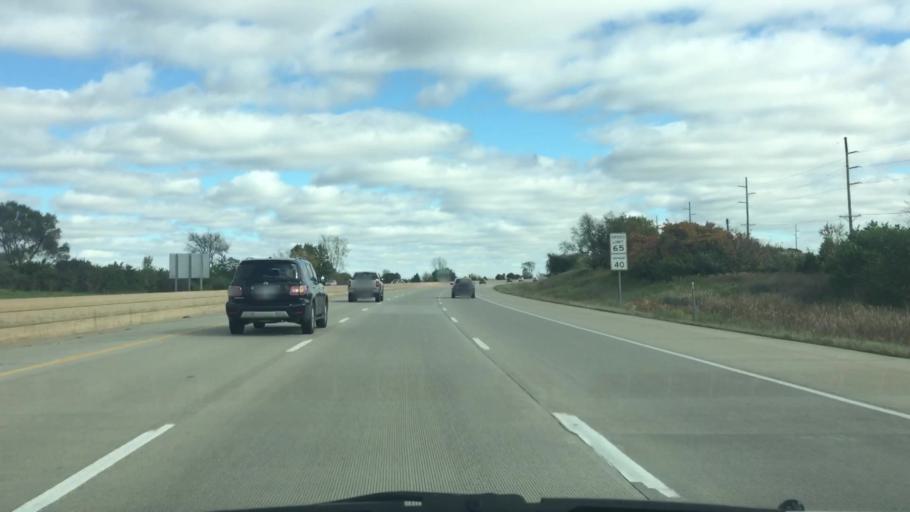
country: US
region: Iowa
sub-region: Johnson County
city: Iowa City
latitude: 41.6862
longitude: -91.4872
